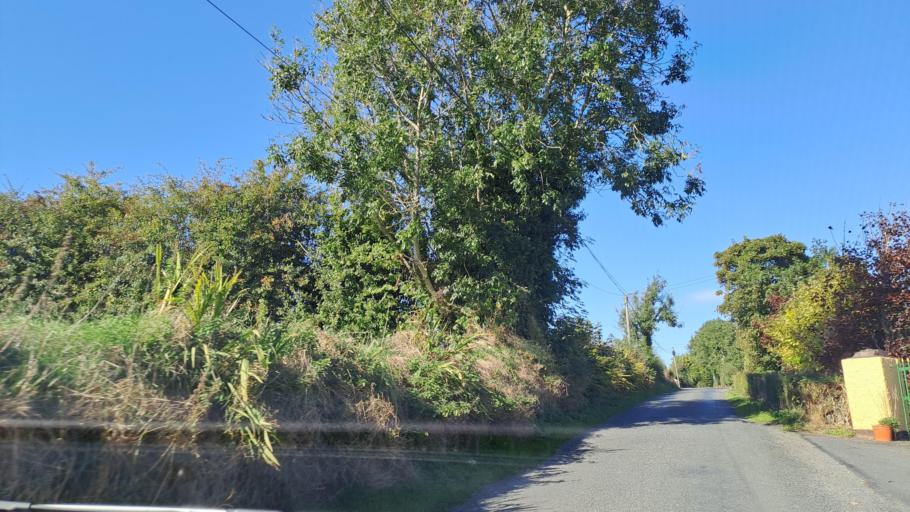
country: IE
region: Ulster
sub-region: County Monaghan
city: Carrickmacross
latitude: 54.0001
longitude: -6.7746
